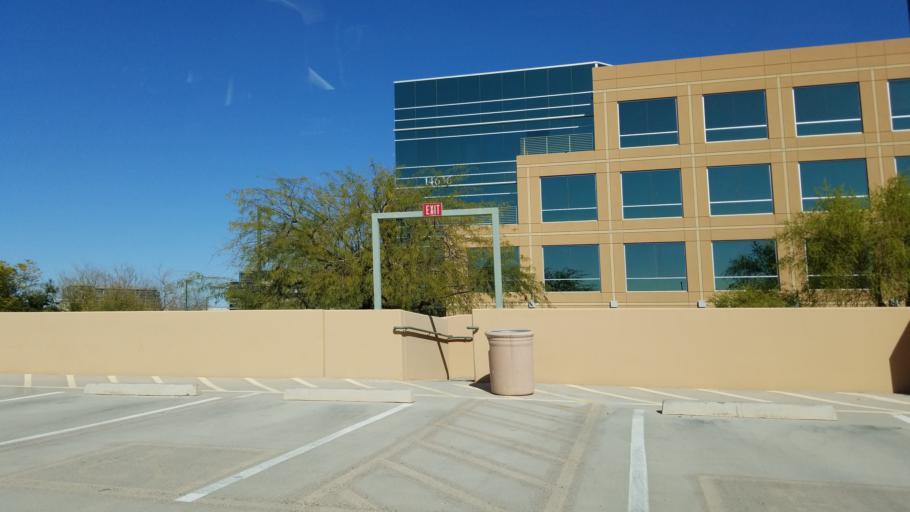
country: US
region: Arizona
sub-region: Maricopa County
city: Paradise Valley
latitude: 33.6193
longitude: -111.9281
